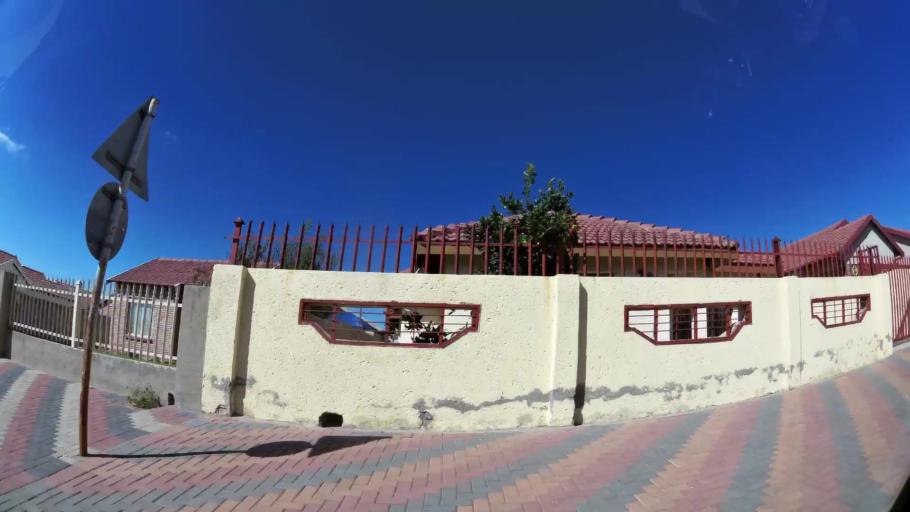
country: ZA
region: Limpopo
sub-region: Capricorn District Municipality
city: Polokwane
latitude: -23.8748
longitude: 29.4126
